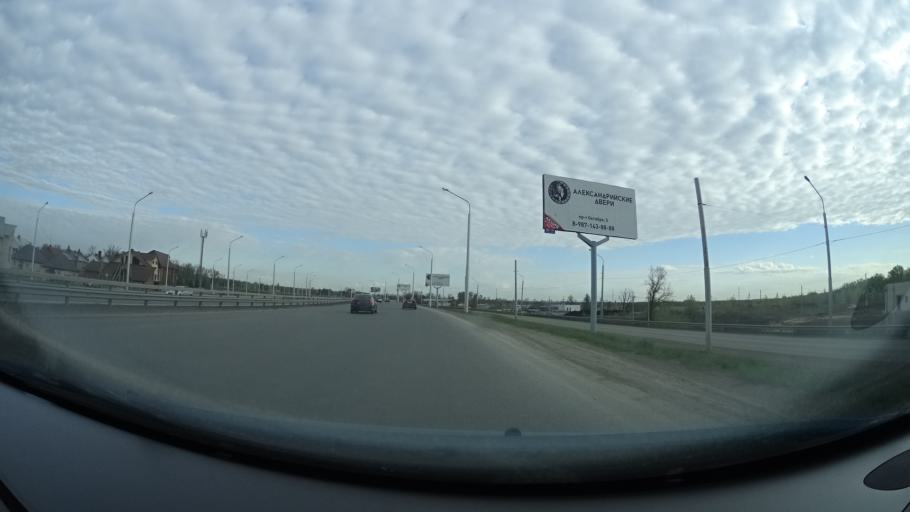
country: RU
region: Bashkortostan
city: Ufa
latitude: 54.7715
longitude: 55.9540
